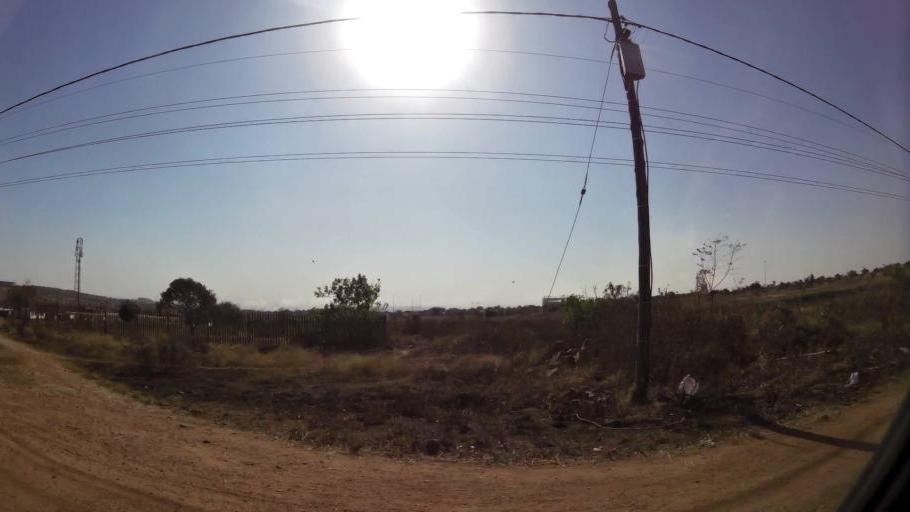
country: ZA
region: Gauteng
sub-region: City of Tshwane Metropolitan Municipality
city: Mabopane
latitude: -25.5295
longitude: 28.0903
